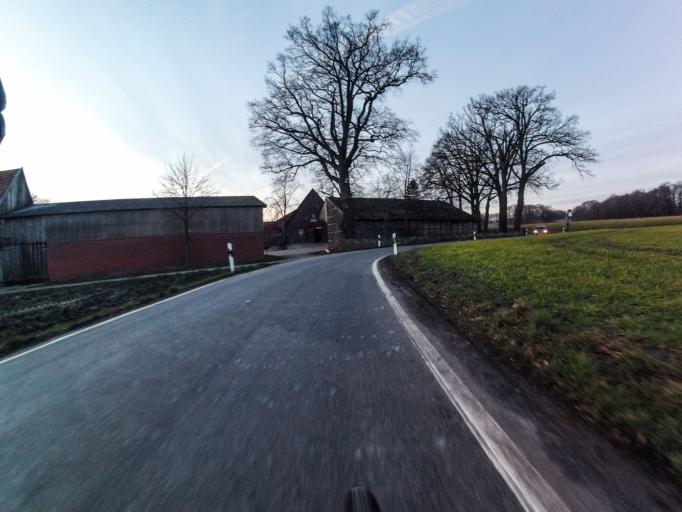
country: DE
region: North Rhine-Westphalia
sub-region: Regierungsbezirk Munster
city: Tecklenburg
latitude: 52.2604
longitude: 7.8083
